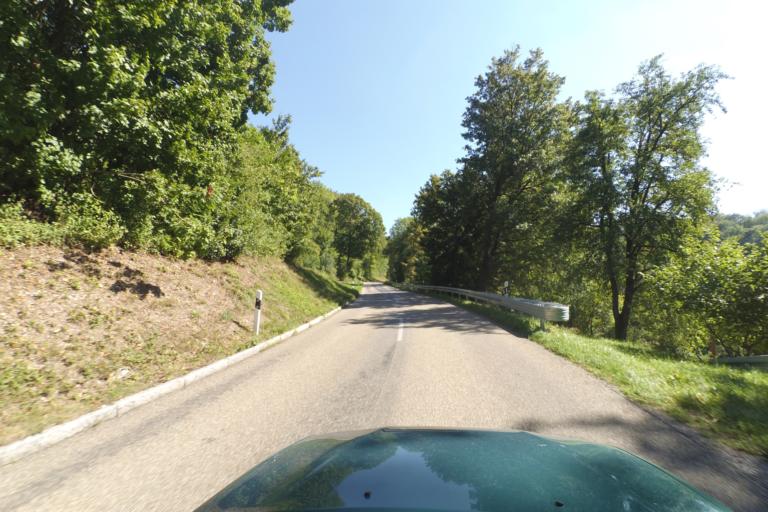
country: DE
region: Baden-Wuerttemberg
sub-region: Regierungsbezirk Stuttgart
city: Langenburg
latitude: 49.2576
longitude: 9.8457
